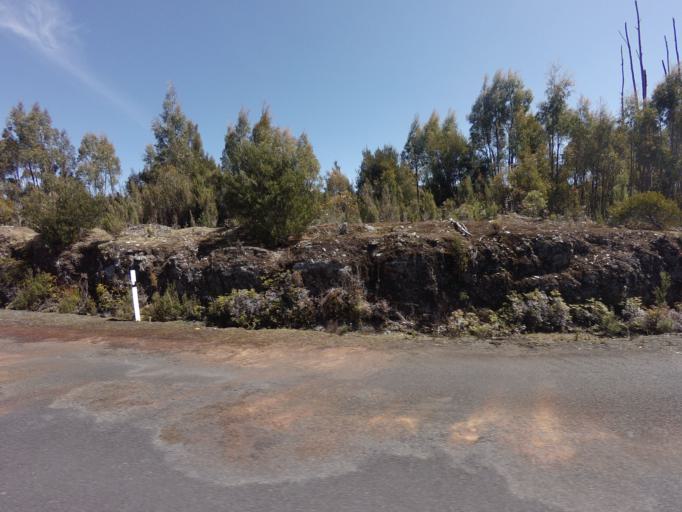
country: AU
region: Tasmania
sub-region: Huon Valley
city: Geeveston
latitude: -42.8067
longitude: 146.0973
